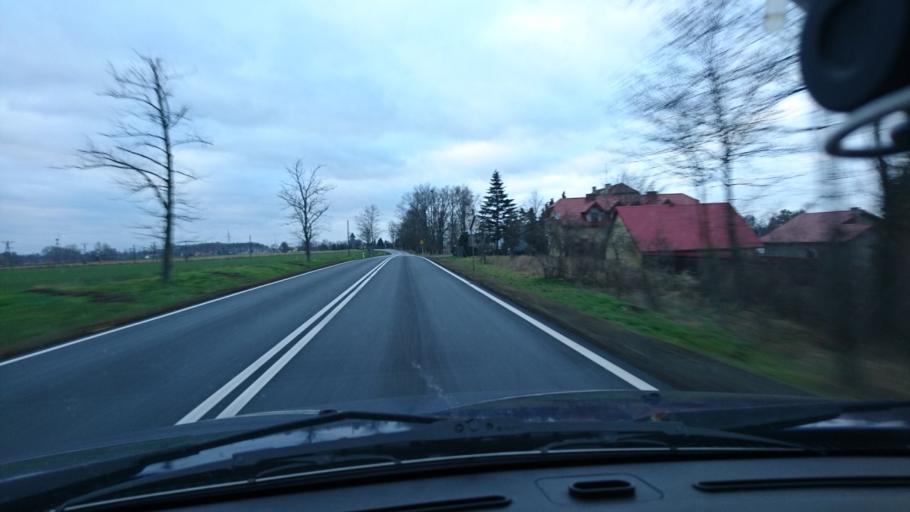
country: PL
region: Lodz Voivodeship
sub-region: Powiat wieruszowski
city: Boleslawiec
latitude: 51.1578
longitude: 18.1676
